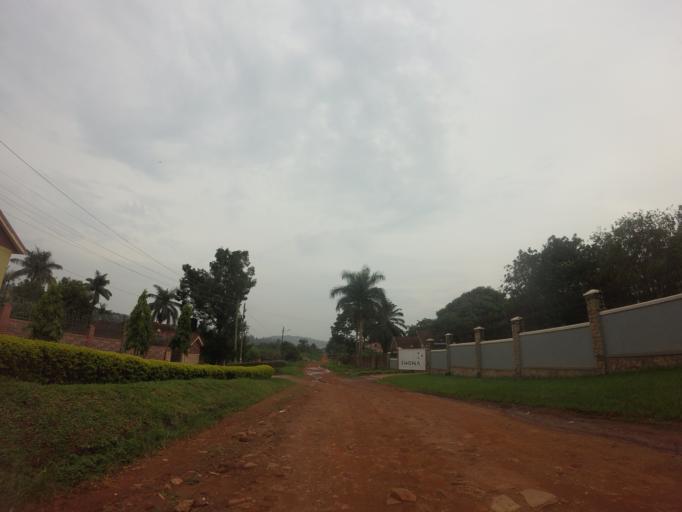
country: UG
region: Central Region
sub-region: Wakiso District
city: Kireka
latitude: 0.3556
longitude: 32.6216
